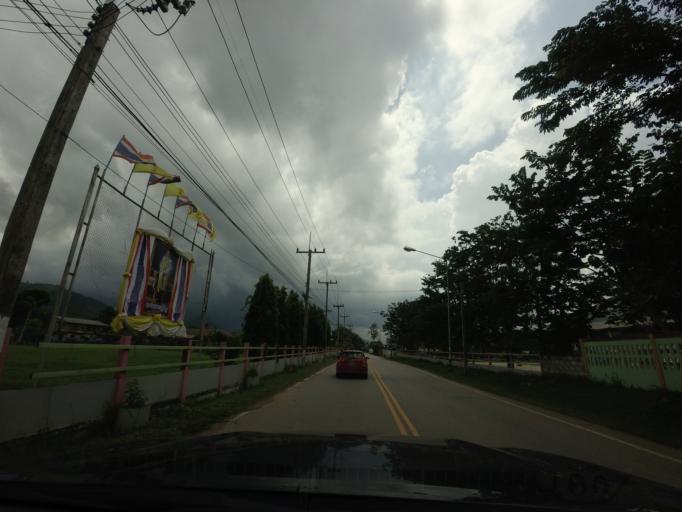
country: LA
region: Vientiane
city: Muang Sanakham
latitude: 18.0036
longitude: 101.7568
